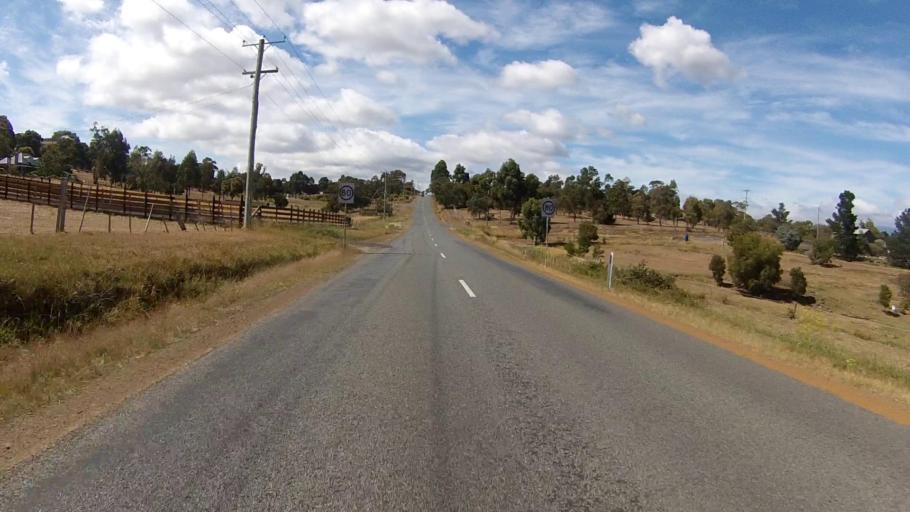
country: AU
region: Tasmania
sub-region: Brighton
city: Bridgewater
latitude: -42.7107
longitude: 147.2699
